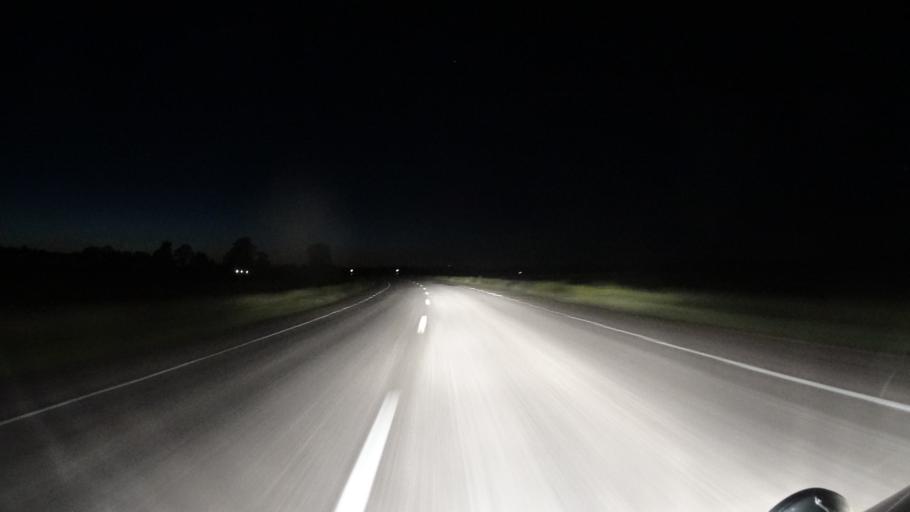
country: SE
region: OEstergoetland
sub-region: Odeshogs Kommun
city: OEdeshoeg
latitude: 58.2473
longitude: 14.7244
